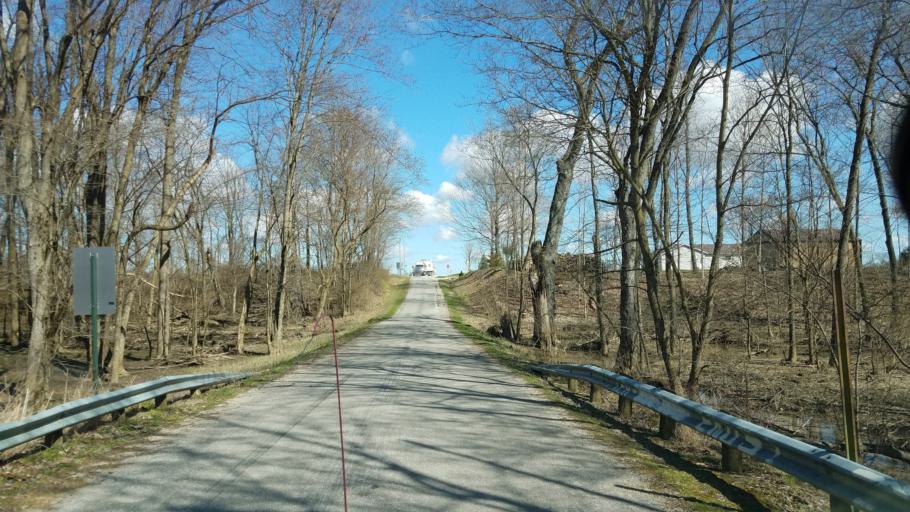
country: US
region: Ohio
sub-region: Sandusky County
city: Mount Carmel
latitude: 41.0650
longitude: -82.9389
